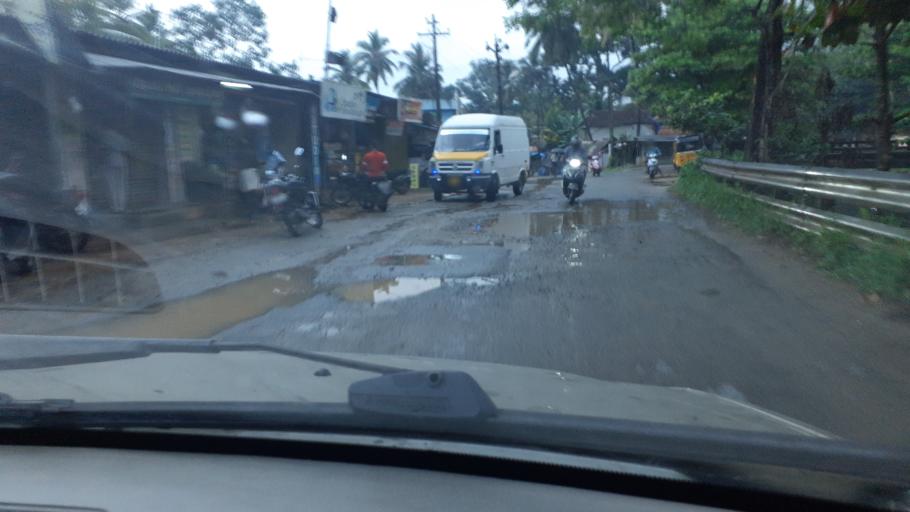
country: IN
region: Tamil Nadu
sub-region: Kanniyakumari
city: Padmanabhapuram
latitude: 8.3626
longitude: 77.3123
